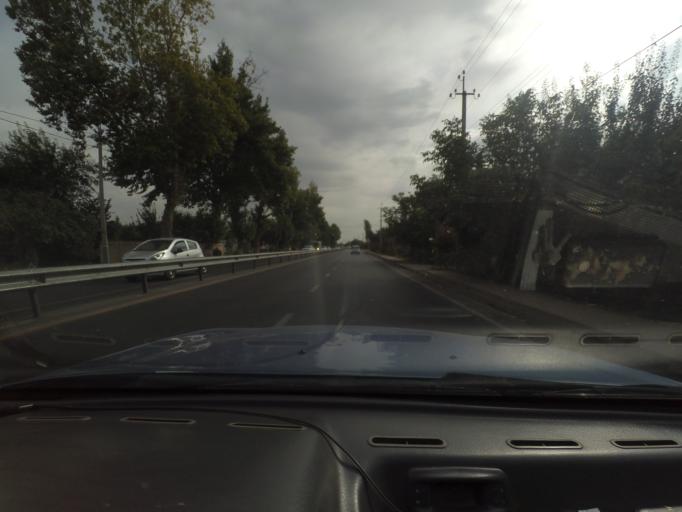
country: UZ
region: Toshkent
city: Qibray
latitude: 41.3987
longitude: 69.4869
